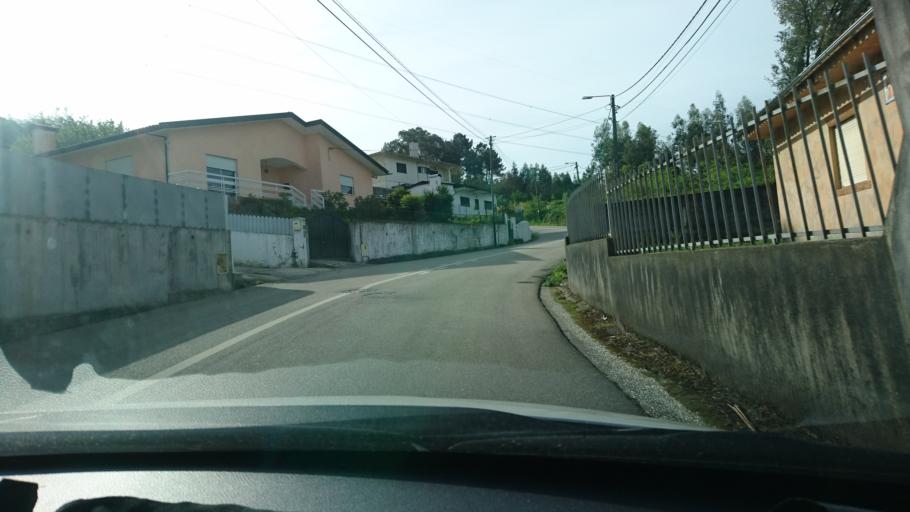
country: PT
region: Aveiro
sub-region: Oliveira de Azemeis
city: Sao Roque
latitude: 40.8784
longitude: -8.4787
